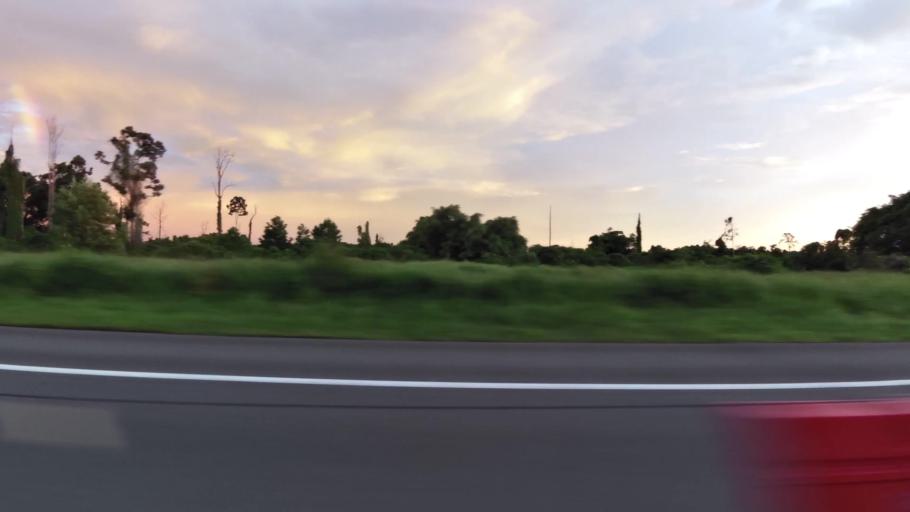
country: BN
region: Belait
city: Kuala Belait
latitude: 4.5787
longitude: 114.2704
